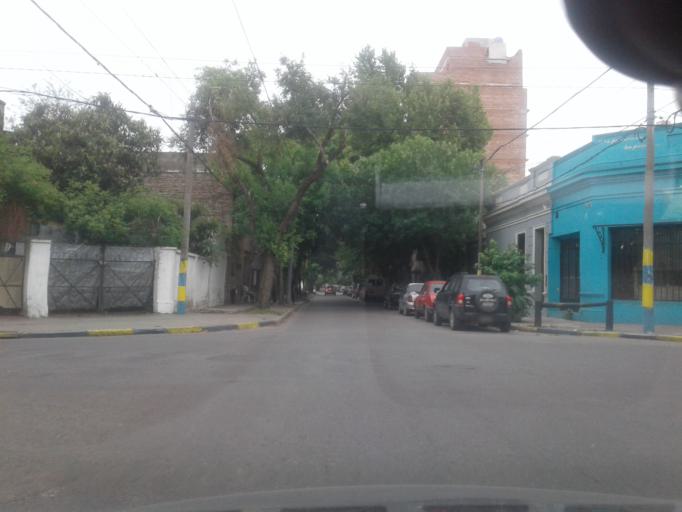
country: AR
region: Santa Fe
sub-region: Departamento de Rosario
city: Rosario
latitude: -32.9162
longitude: -60.6803
